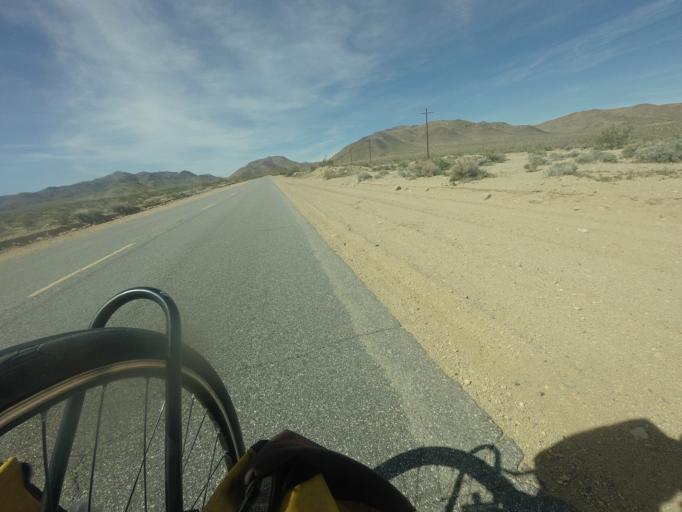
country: US
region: California
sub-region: San Bernardino County
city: Searles Valley
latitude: 35.5720
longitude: -117.4460
